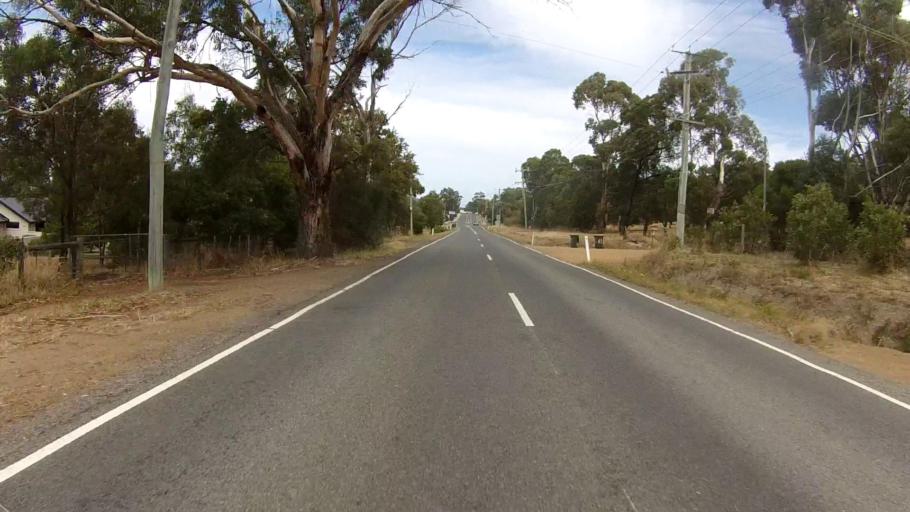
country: AU
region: Tasmania
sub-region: Clarence
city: Lauderdale
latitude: -42.9011
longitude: 147.4791
